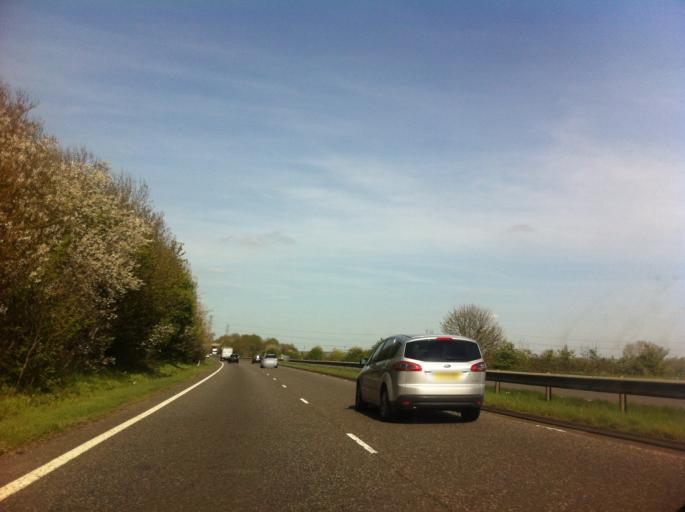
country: GB
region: England
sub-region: Northamptonshire
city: Earls Barton
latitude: 52.2574
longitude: -0.7406
